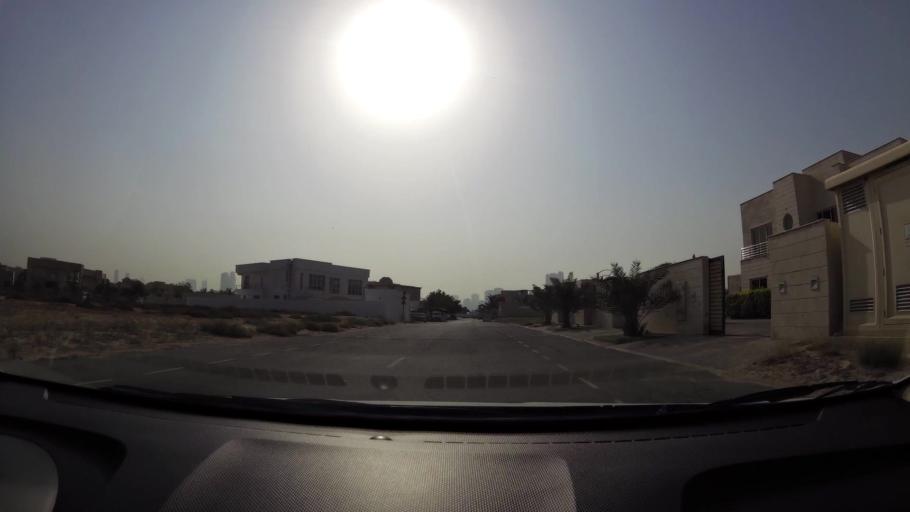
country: AE
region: Ash Shariqah
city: Sharjah
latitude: 25.3077
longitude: 55.3427
